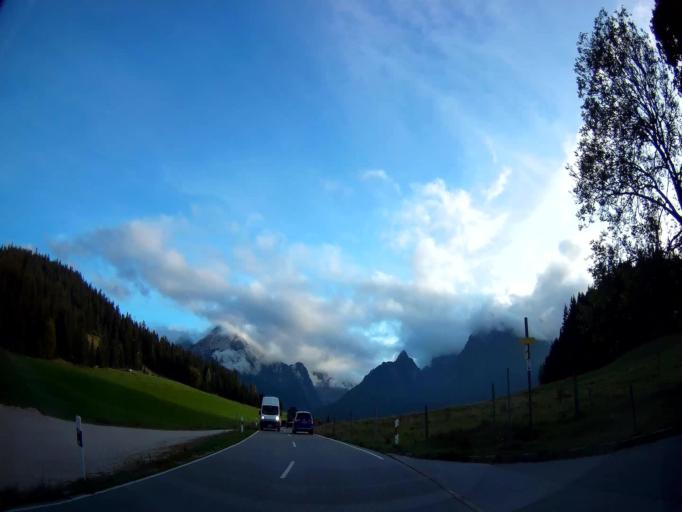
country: DE
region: Bavaria
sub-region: Upper Bavaria
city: Ramsau
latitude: 47.6263
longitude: 12.9045
